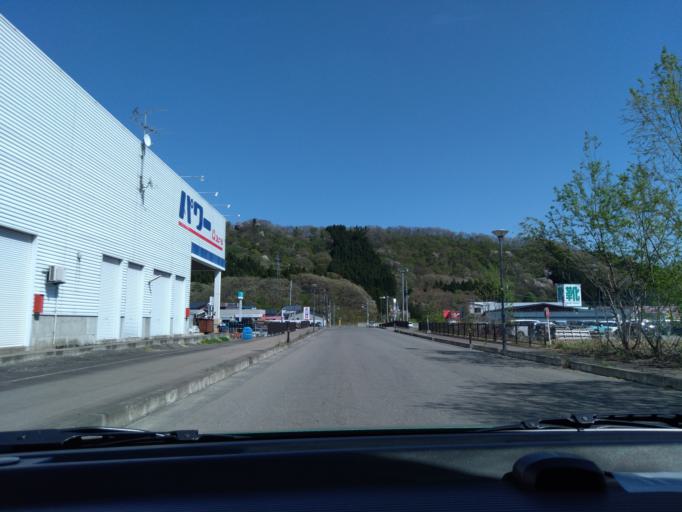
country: JP
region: Akita
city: Kakunodatemachi
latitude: 39.5911
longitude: 140.5725
